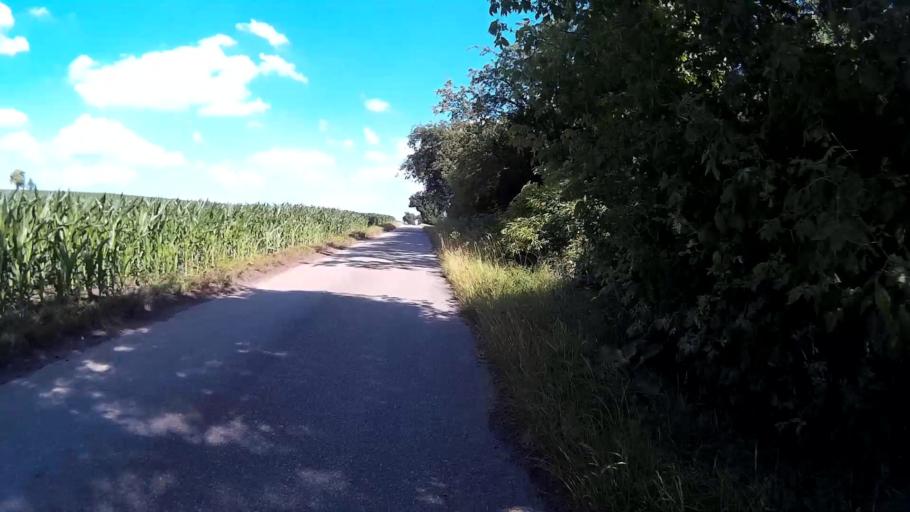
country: CZ
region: South Moravian
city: Moutnice
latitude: 49.0390
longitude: 16.7156
